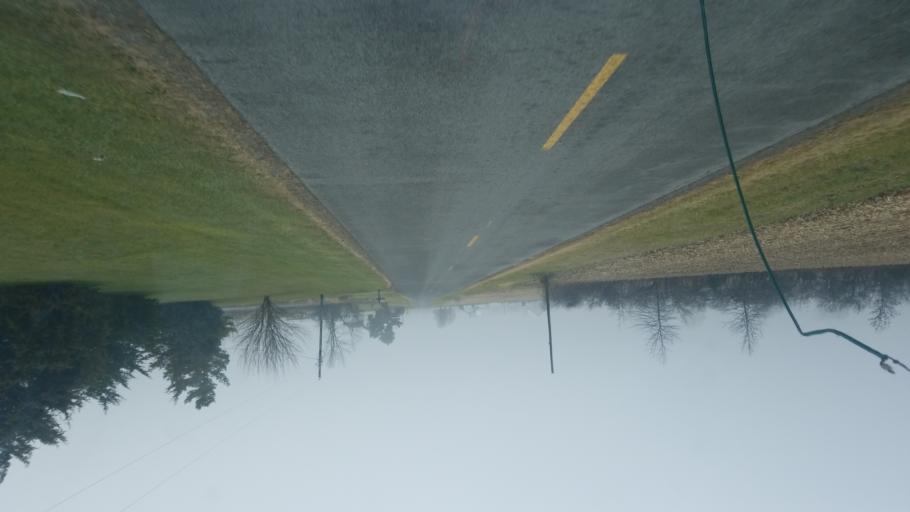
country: US
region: Ohio
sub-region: Logan County
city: Northwood
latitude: 40.4676
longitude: -83.5445
